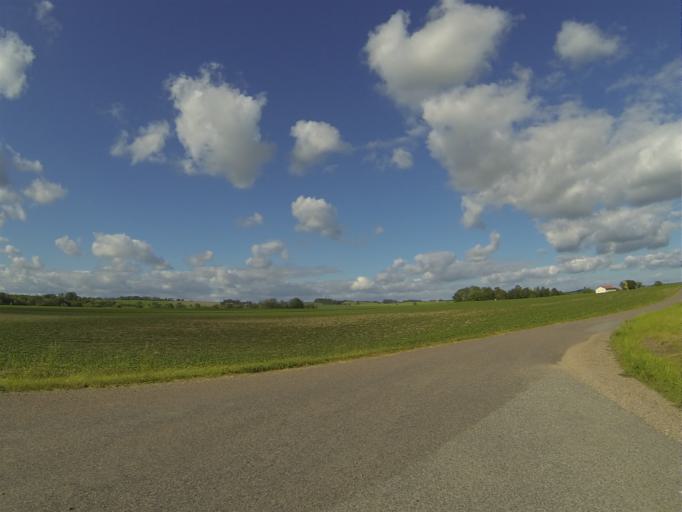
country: SE
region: Skane
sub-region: Staffanstorps Kommun
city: Staffanstorp
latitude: 55.6784
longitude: 13.2603
